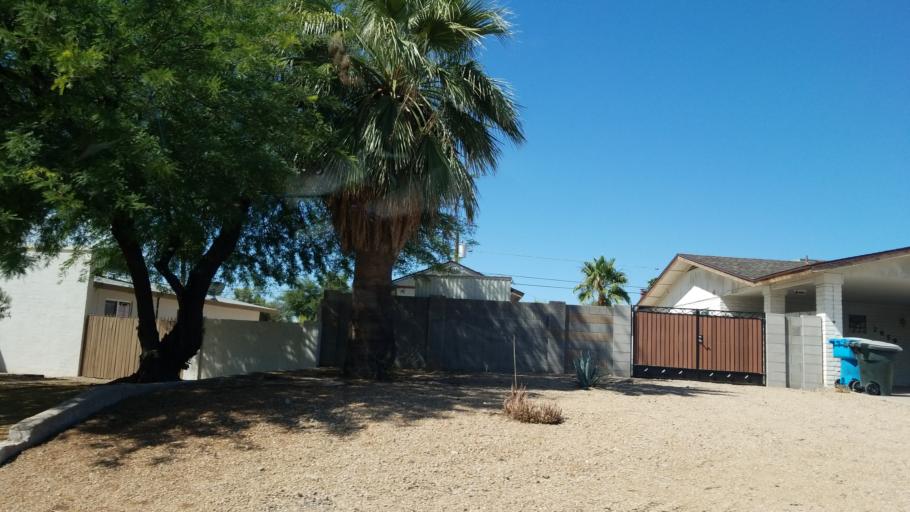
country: US
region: Arizona
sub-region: Maricopa County
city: Paradise Valley
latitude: 33.6104
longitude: -112.0193
